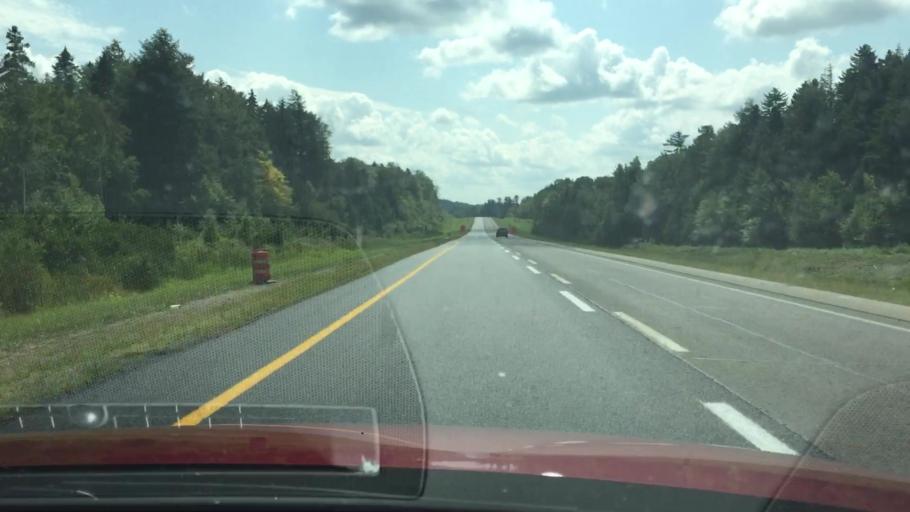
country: US
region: Maine
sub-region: Penobscot County
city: Medway
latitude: 45.7270
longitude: -68.4735
